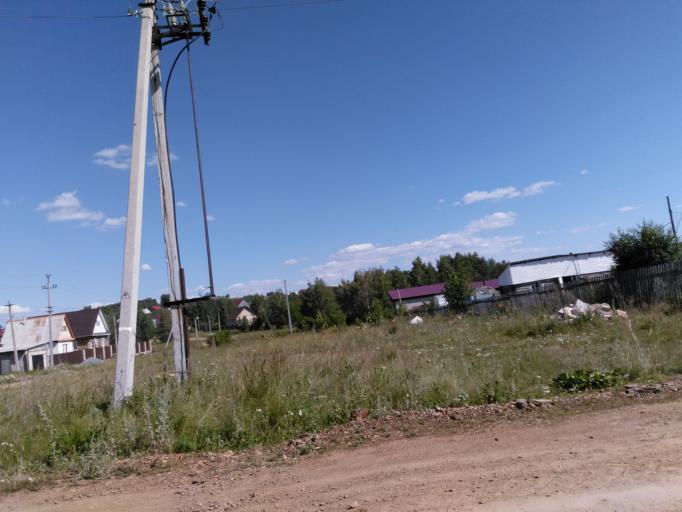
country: RU
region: Bashkortostan
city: Uchaly
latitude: 54.2919
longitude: 59.3660
